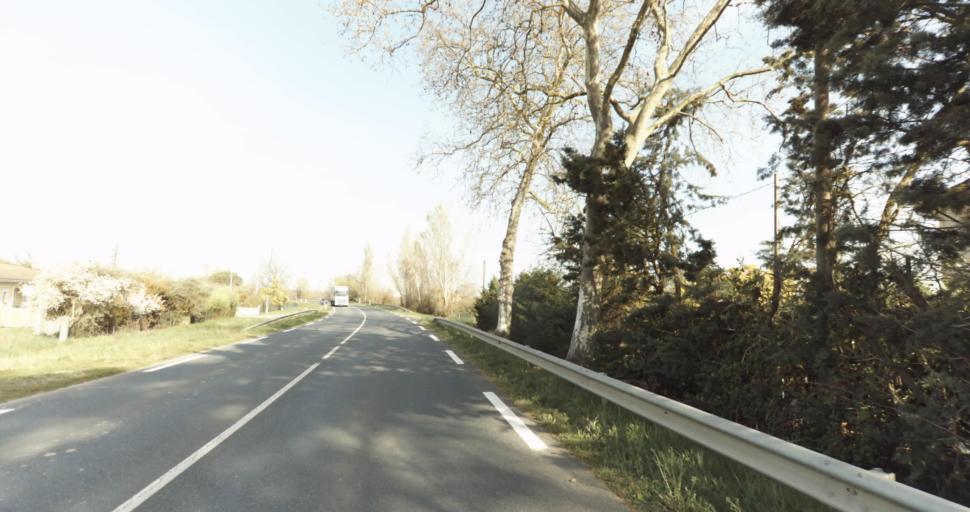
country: FR
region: Midi-Pyrenees
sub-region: Departement du Tarn
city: Giroussens
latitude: 43.7499
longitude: 1.7295
